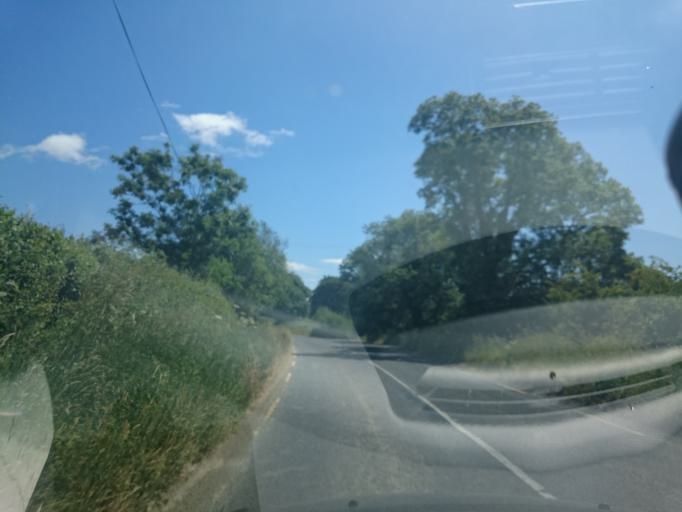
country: IE
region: Leinster
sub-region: County Carlow
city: Bagenalstown
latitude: 52.6273
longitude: -7.0242
